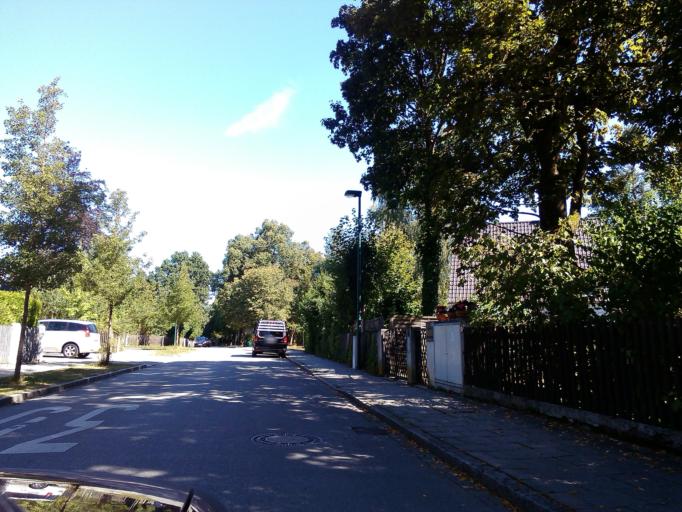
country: DE
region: Bavaria
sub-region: Upper Bavaria
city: Grafelfing
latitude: 48.1308
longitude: 11.4285
